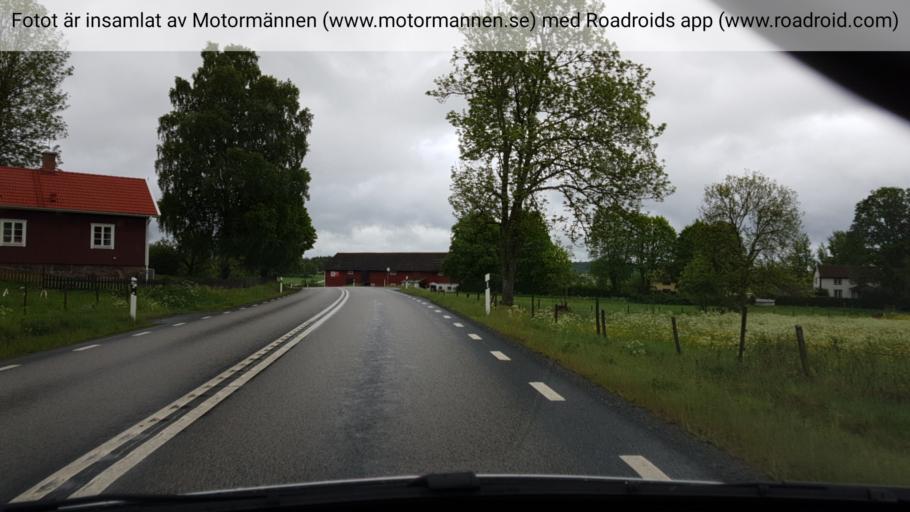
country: SE
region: Joenkoeping
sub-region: Jonkopings Kommun
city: Huskvarna
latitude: 57.7754
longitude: 14.3737
